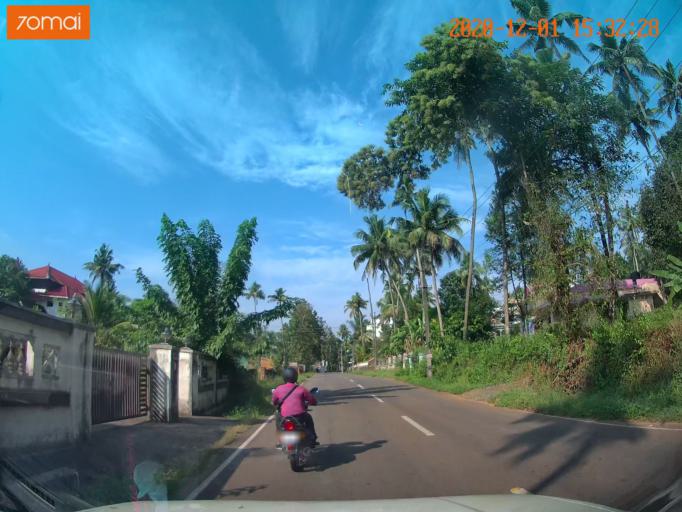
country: IN
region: Kerala
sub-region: Ernakulam
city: Muvattupuzha
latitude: 9.9728
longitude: 76.5739
